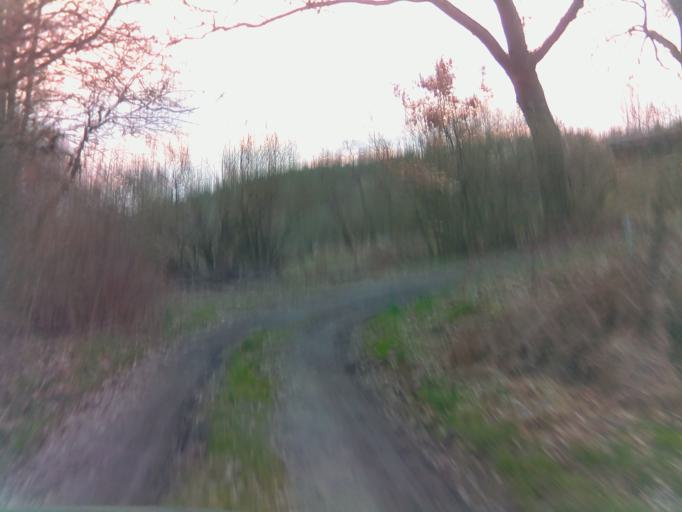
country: DE
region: Brandenburg
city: Jamlitz
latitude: 51.9819
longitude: 14.4095
